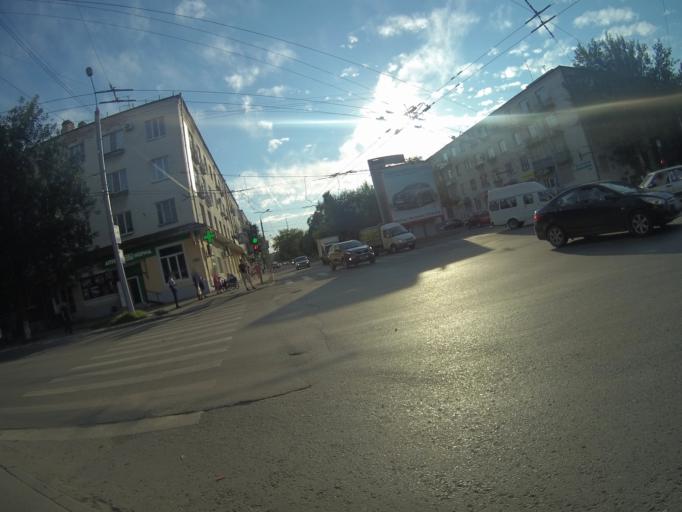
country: RU
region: Vladimir
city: Vladimir
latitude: 56.1456
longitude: 40.4243
